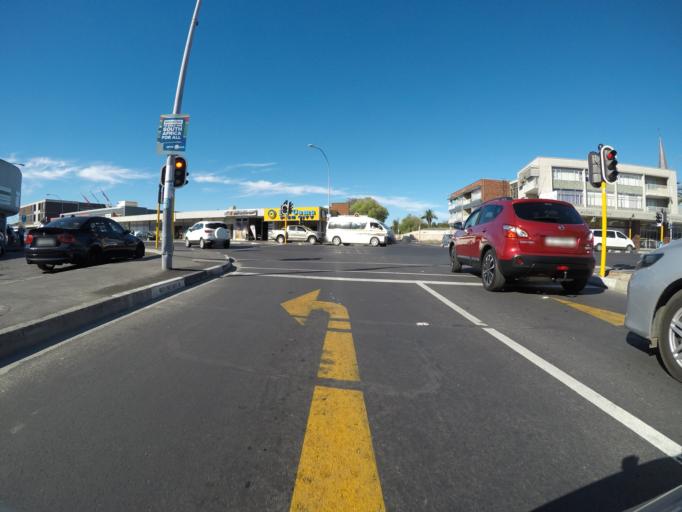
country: ZA
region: Western Cape
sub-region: City of Cape Town
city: Kraaifontein
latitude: -33.9241
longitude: 18.6776
